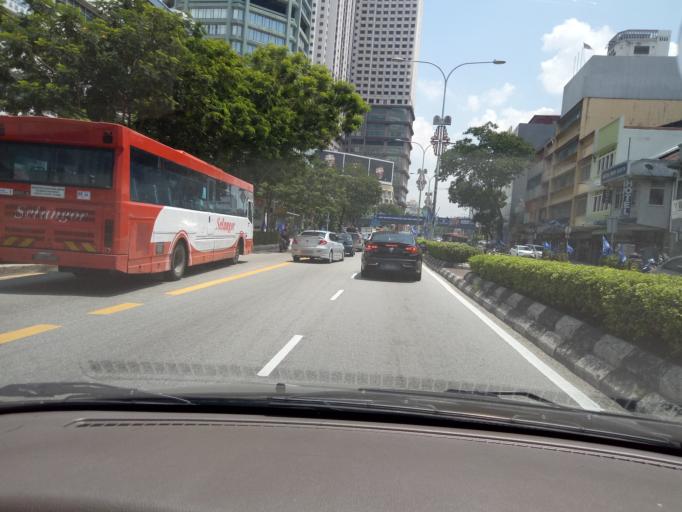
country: MY
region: Kuala Lumpur
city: Kuala Lumpur
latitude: 3.1708
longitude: 101.6939
